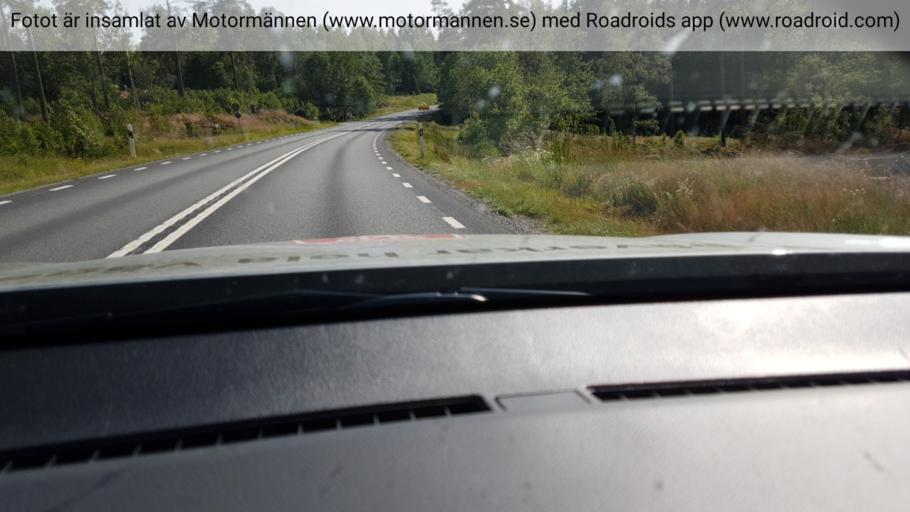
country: SE
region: Joenkoeping
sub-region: Aneby Kommun
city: Aneby
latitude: 57.9190
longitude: 14.9094
